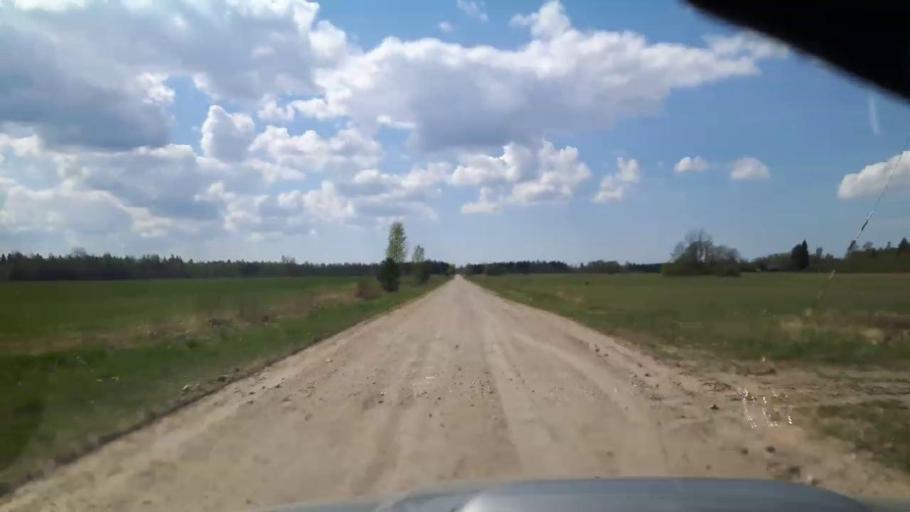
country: EE
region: Paernumaa
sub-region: Tootsi vald
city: Tootsi
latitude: 58.4641
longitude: 24.8890
